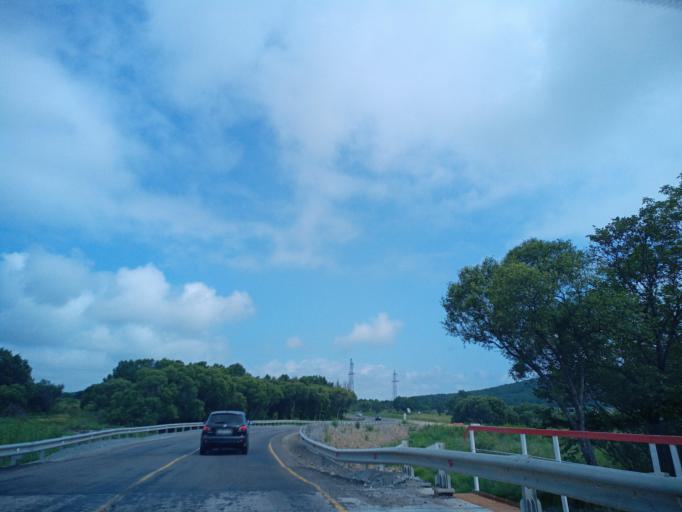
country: RU
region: Primorskiy
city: Dal'nerechensk
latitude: 46.0670
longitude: 133.8952
